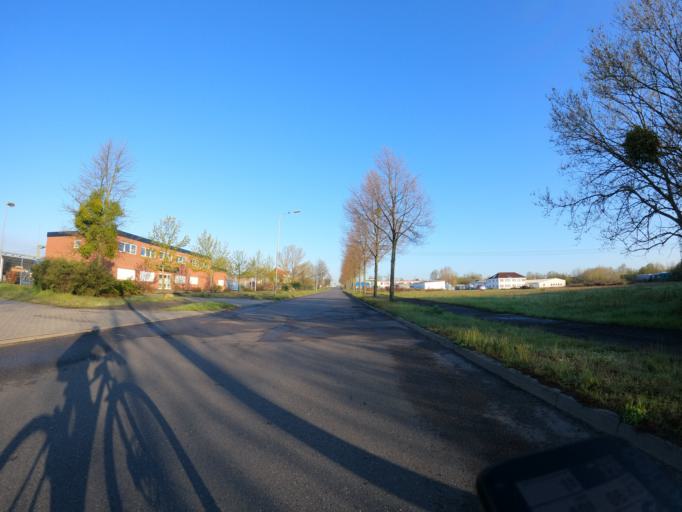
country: DE
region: Brandenburg
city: Altlandsberg
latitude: 52.5426
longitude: 13.7131
